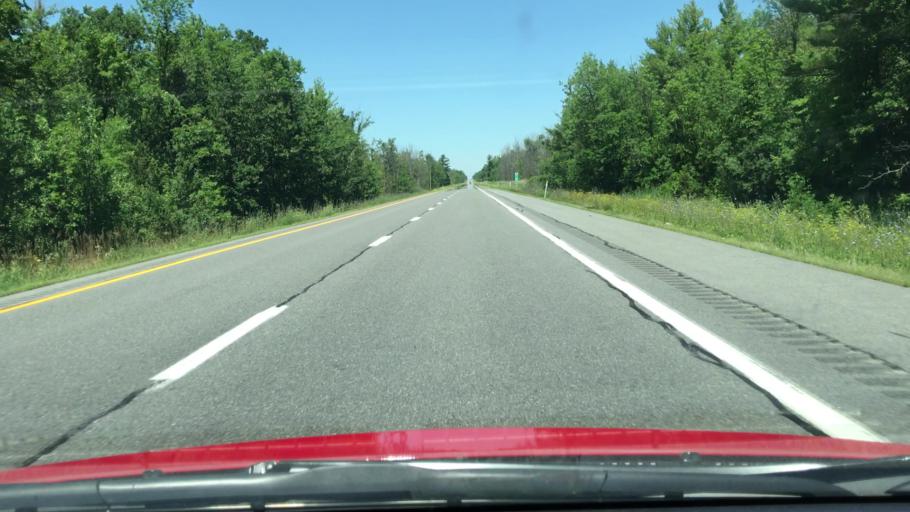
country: US
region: New York
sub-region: Clinton County
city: Champlain
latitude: 44.9364
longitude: -73.4468
